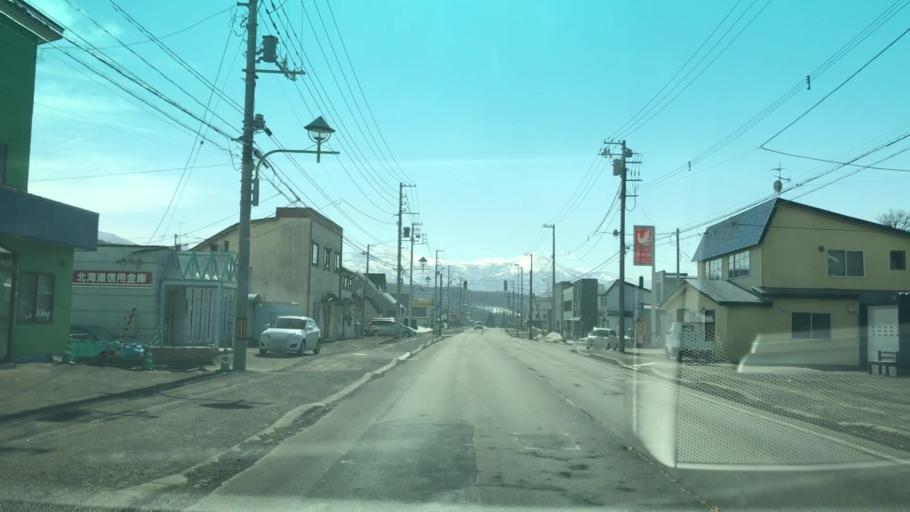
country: JP
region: Hokkaido
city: Iwanai
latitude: 42.9822
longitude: 140.6508
